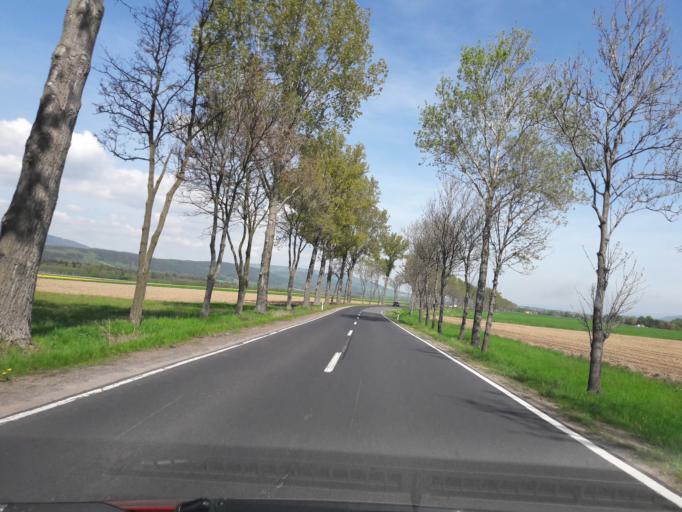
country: PL
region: Lower Silesian Voivodeship
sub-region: Powiat klodzki
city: Bystrzyca Klodzka
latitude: 50.2442
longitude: 16.6710
